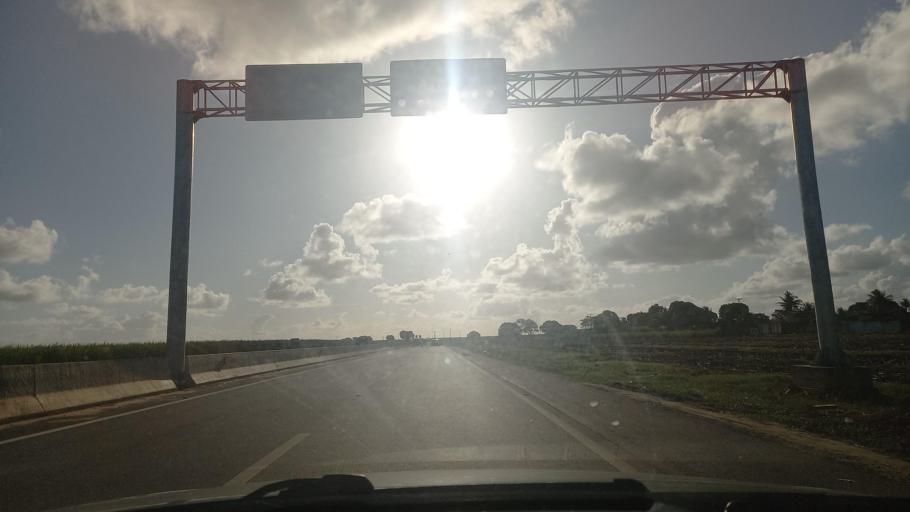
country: BR
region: Alagoas
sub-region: Sao Miguel Dos Campos
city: Sao Miguel dos Campos
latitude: -9.8077
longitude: -36.1174
